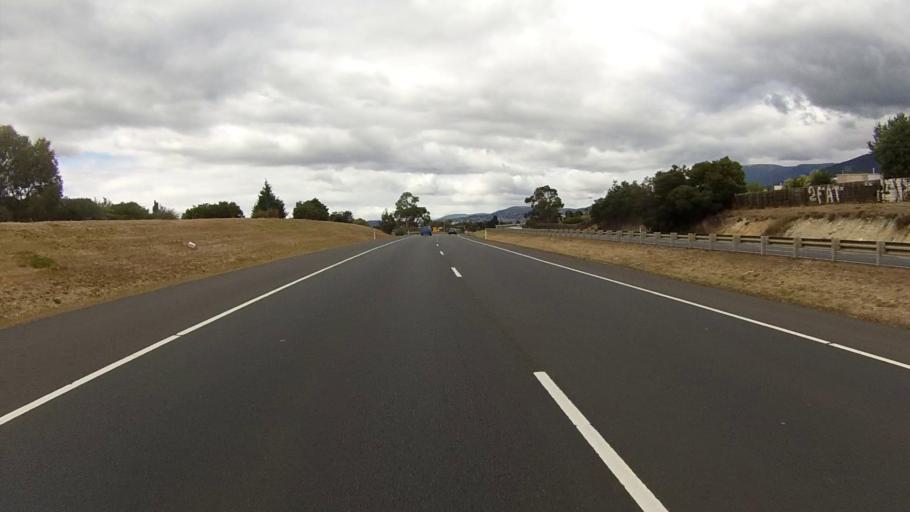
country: AU
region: Tasmania
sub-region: Glenorchy
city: Claremont
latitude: -42.7860
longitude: 147.2429
